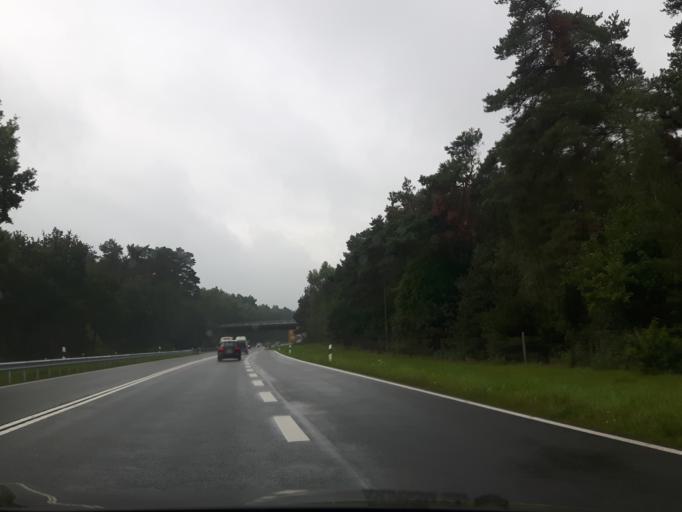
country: DE
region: Lower Saxony
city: Lingen
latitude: 52.5000
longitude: 7.3388
